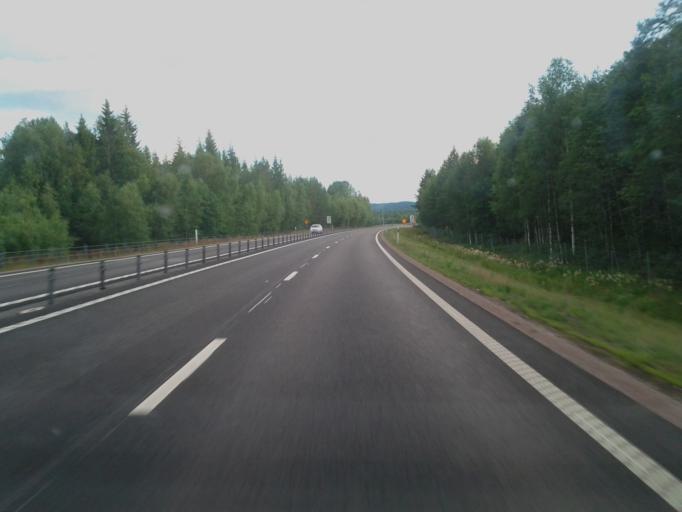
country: SE
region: Dalarna
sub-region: Borlange Kommun
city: Borlaenge
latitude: 60.4413
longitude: 15.3626
